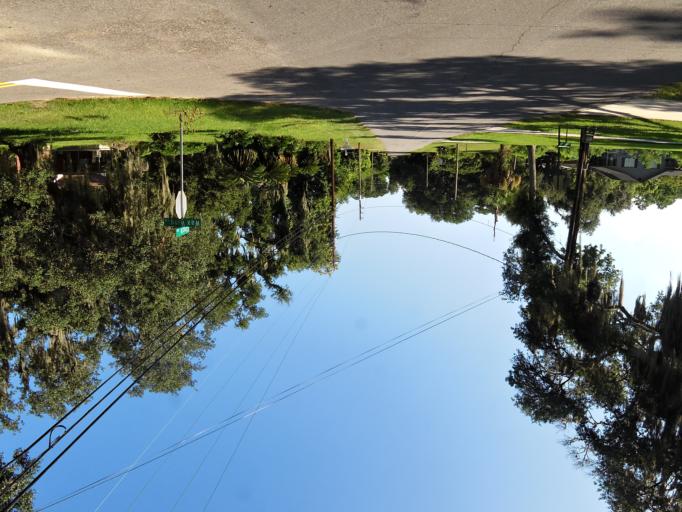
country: US
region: Florida
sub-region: Nassau County
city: Fernandina Beach
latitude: 30.6418
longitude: -81.4629
